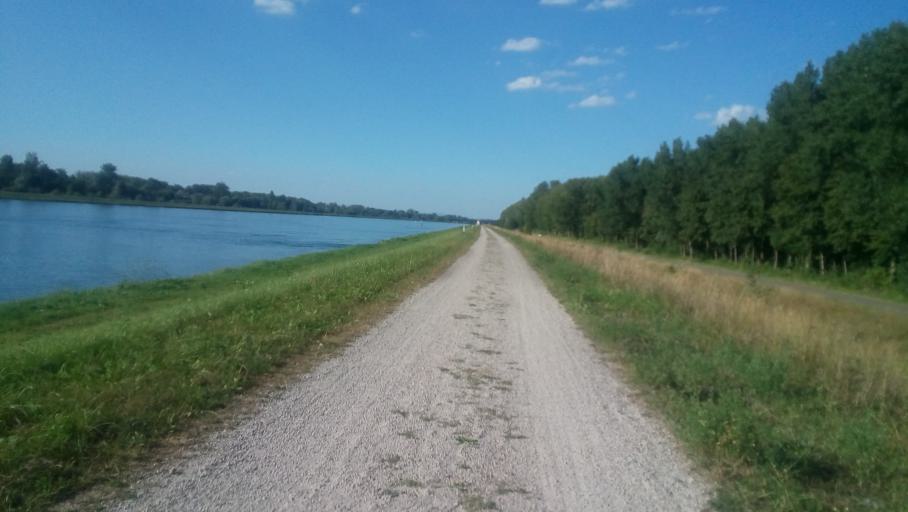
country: DE
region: Baden-Wuerttemberg
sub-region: Karlsruhe Region
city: Lichtenau
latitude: 48.7307
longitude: 7.9697
